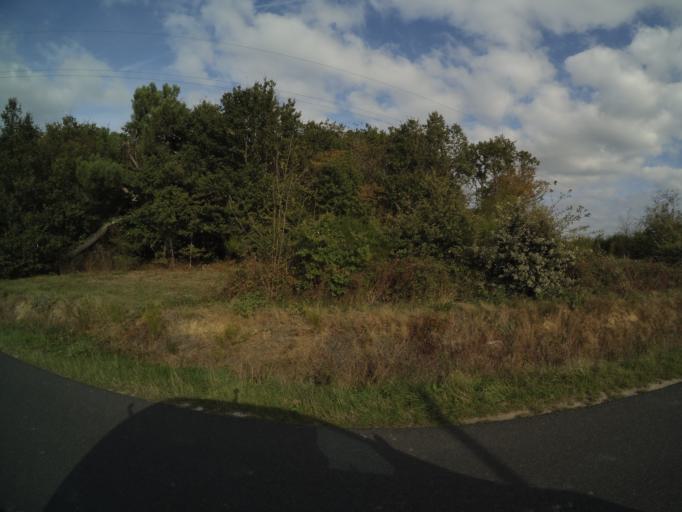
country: FR
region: Centre
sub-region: Departement d'Indre-et-Loire
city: Nazelles-Negron
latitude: 47.4691
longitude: 0.9547
